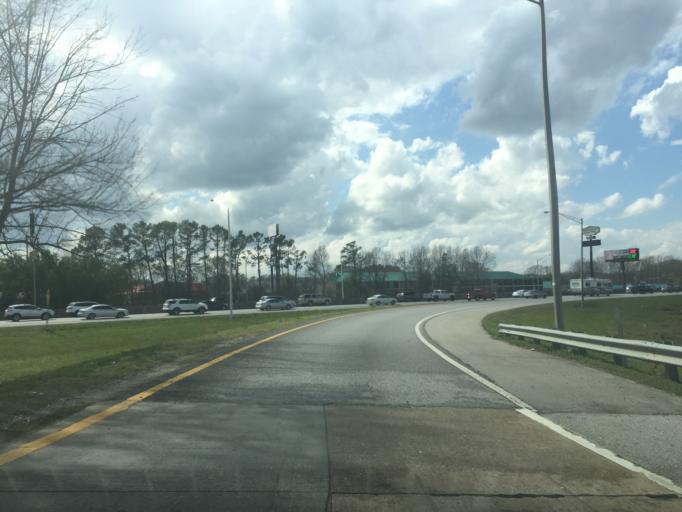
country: US
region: Georgia
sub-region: Catoosa County
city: Indian Springs
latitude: 34.9917
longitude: -85.2039
